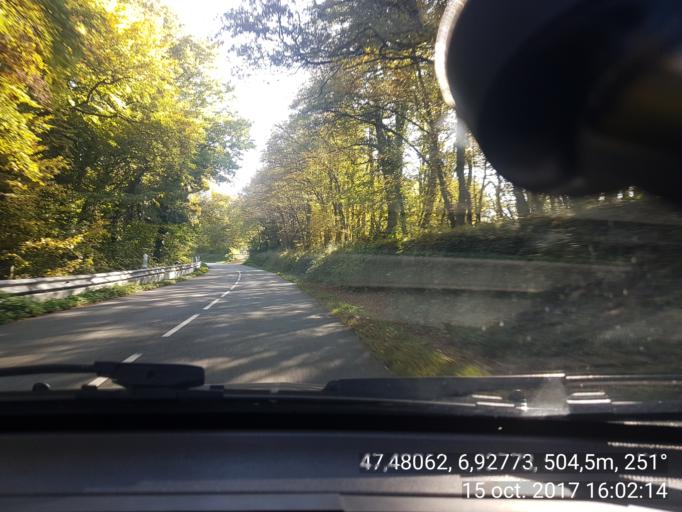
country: FR
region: Franche-Comte
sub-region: Territoire de Belfort
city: Beaucourt
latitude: 47.4806
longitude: 6.9278
